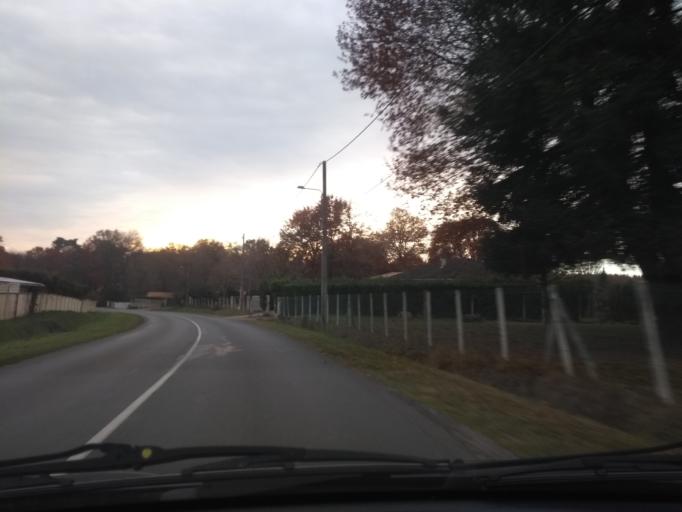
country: FR
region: Aquitaine
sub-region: Departement de la Gironde
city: Saucats
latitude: 44.6511
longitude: -0.6072
